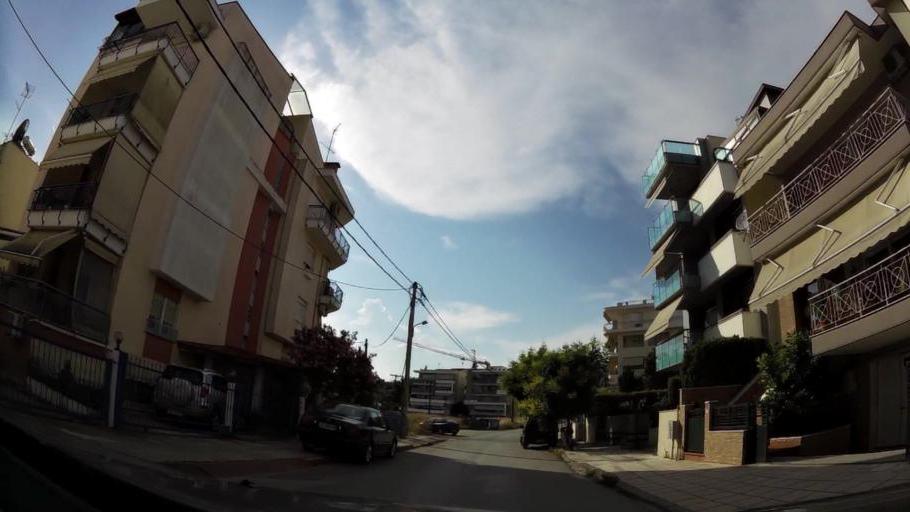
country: GR
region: Central Macedonia
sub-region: Nomos Thessalonikis
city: Kalamaria
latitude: 40.5765
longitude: 22.9568
